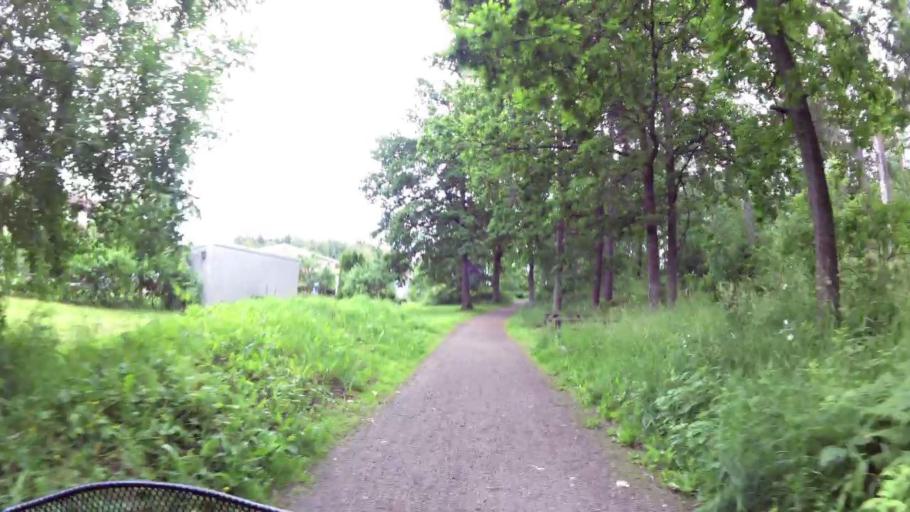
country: SE
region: OEstergoetland
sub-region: Linkopings Kommun
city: Linkoping
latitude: 58.3694
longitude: 15.6705
